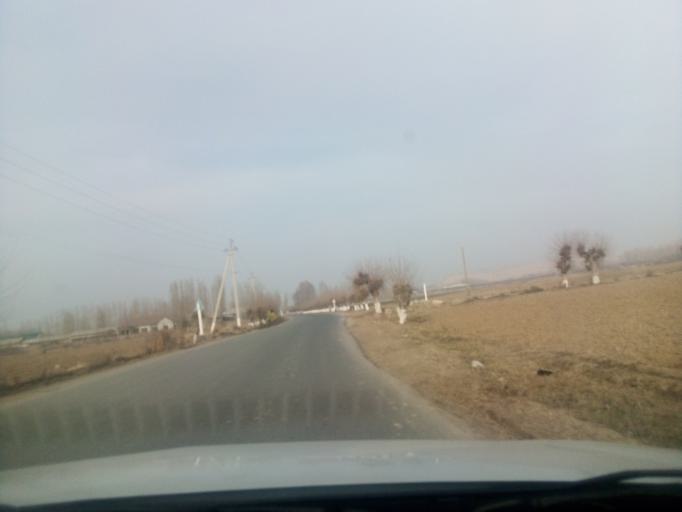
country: UZ
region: Namangan
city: Pop Shahri
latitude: 40.9737
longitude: 71.0995
